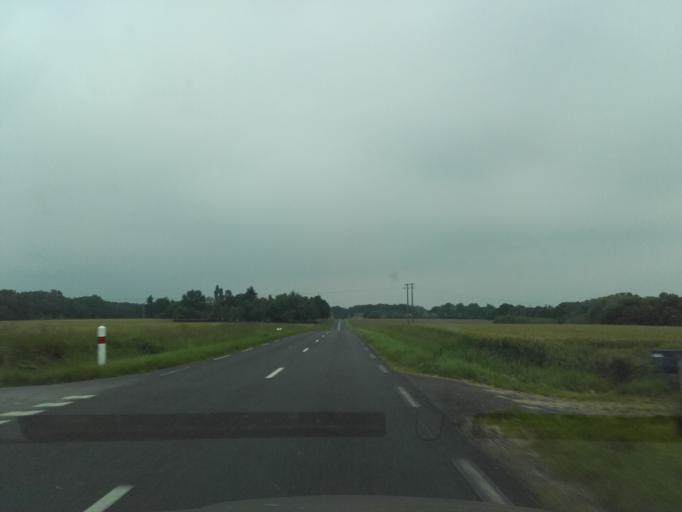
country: FR
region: Centre
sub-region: Departement d'Indre-et-Loire
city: Cerelles
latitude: 47.5119
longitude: 0.6956
